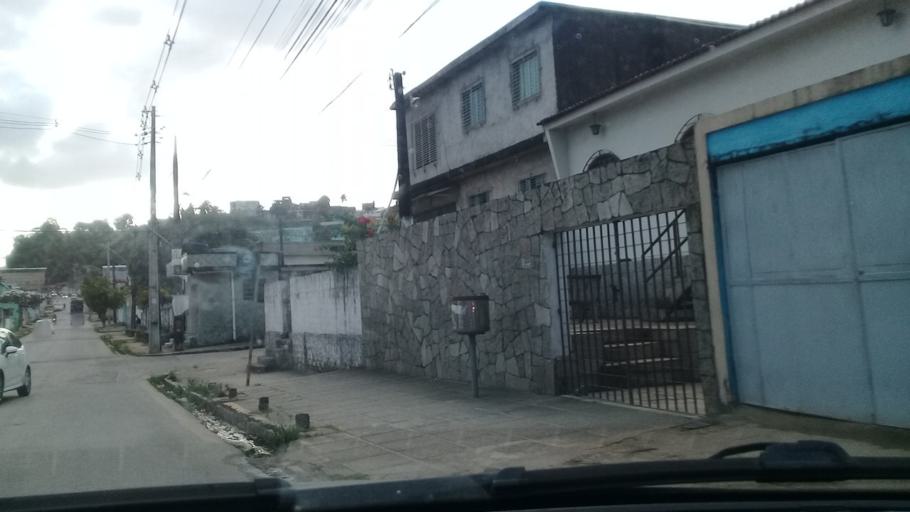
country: BR
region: Pernambuco
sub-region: Jaboatao Dos Guararapes
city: Jaboatao
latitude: -8.1372
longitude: -34.9409
